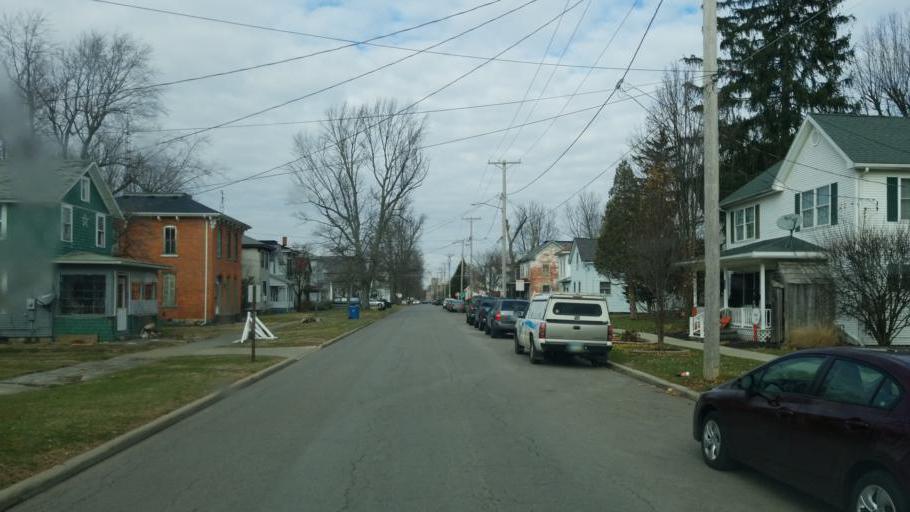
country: US
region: Ohio
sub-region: Crawford County
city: Galion
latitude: 40.7286
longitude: -82.7930
